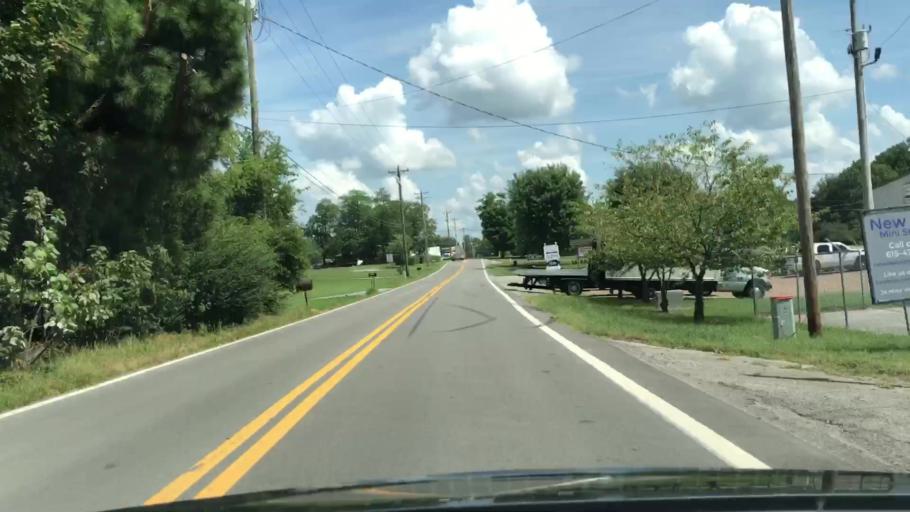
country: US
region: Tennessee
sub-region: Sumner County
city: Portland
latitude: 36.5163
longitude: -86.5679
